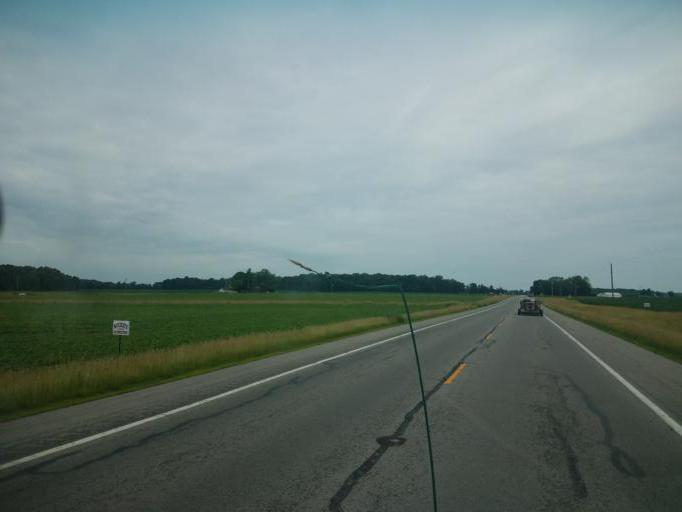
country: US
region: Ohio
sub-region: Hardin County
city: Ada
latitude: 40.7249
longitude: -83.7811
